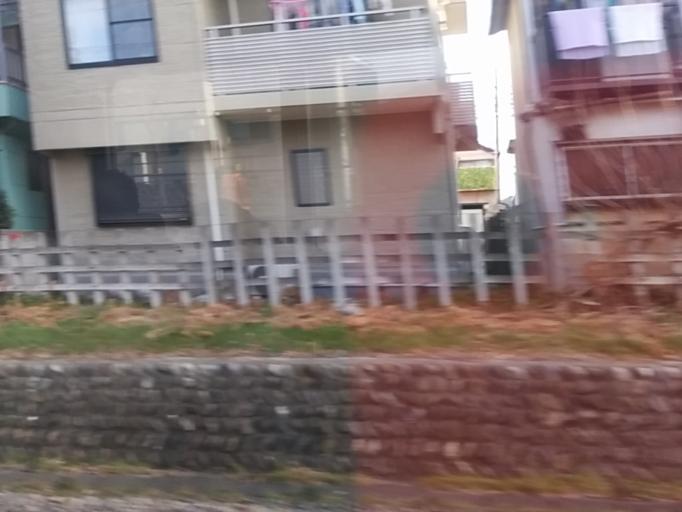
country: JP
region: Saitama
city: Kamifukuoka
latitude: 35.8773
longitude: 139.5090
